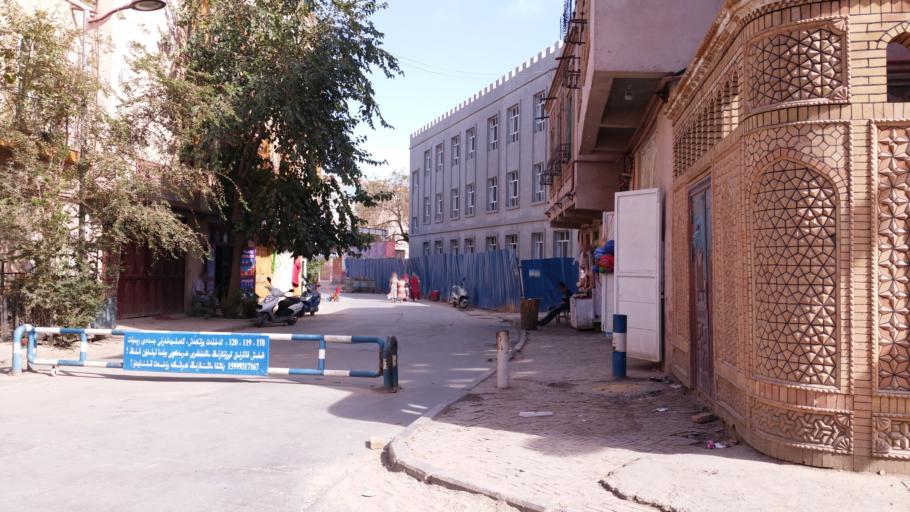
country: CN
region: Xinjiang Uygur Zizhiqu
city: Kashi
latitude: 39.4687
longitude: 75.9886
